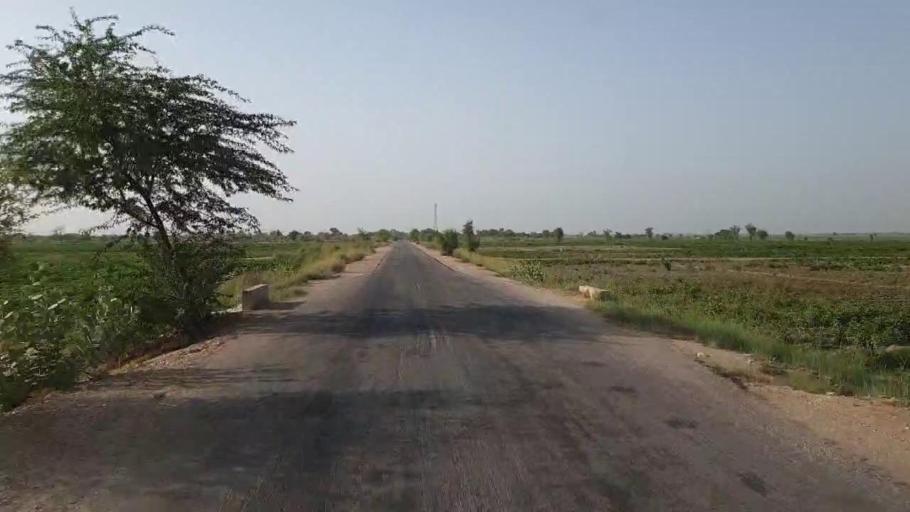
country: PK
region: Sindh
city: Jam Sahib
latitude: 26.4739
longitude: 68.8597
